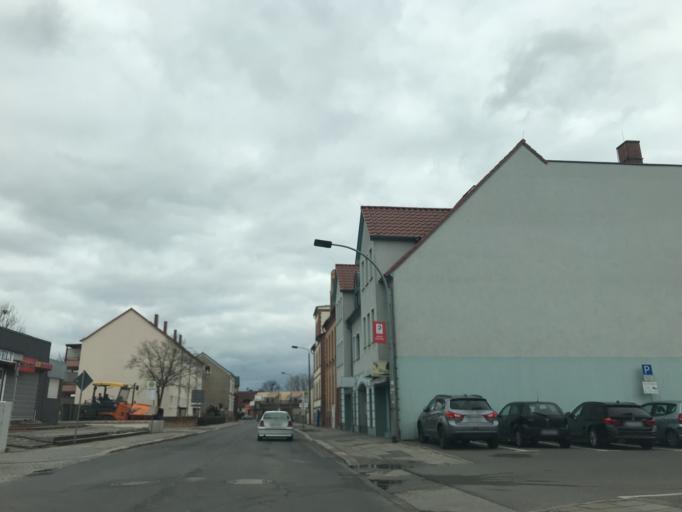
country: DE
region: Brandenburg
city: Luebben
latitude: 51.9424
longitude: 13.8928
